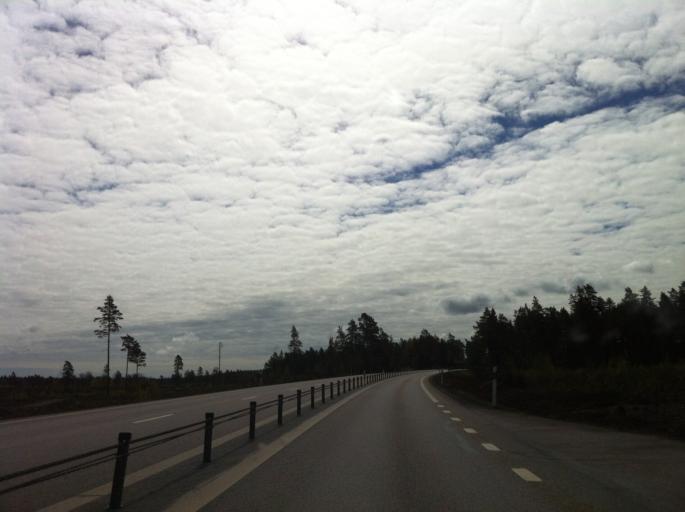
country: SE
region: OEstergoetland
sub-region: Valdemarsviks Kommun
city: Valdemarsvik
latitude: 58.1851
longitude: 16.5811
